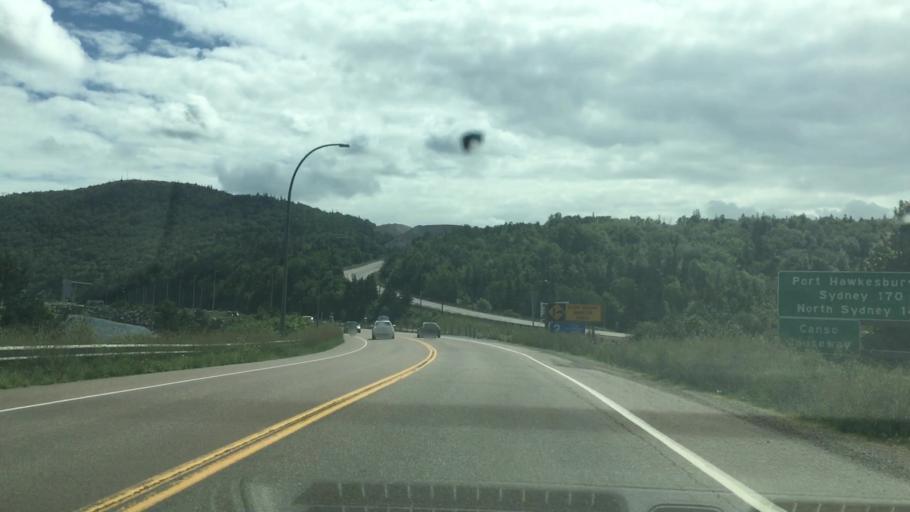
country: CA
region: Nova Scotia
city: Port Hawkesbury
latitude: 45.6460
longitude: -61.4353
